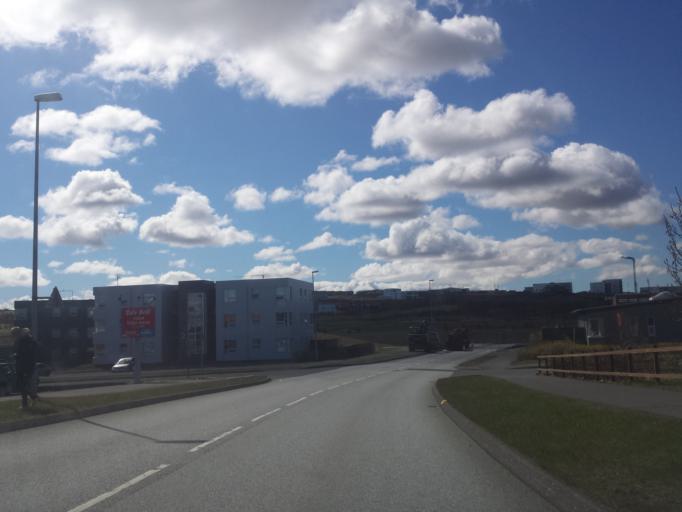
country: IS
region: Capital Region
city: Reykjavik
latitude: 64.0907
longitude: -21.8438
